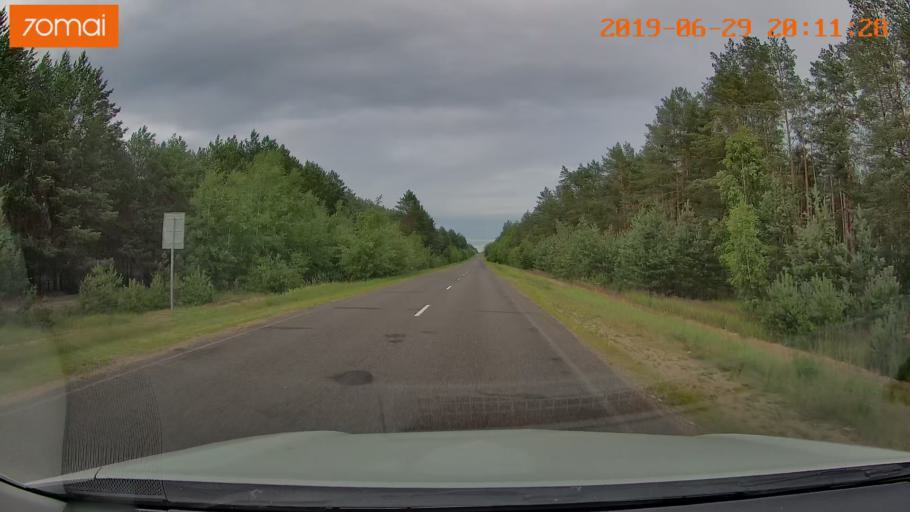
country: BY
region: Brest
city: Lahishyn
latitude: 52.3586
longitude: 26.1144
